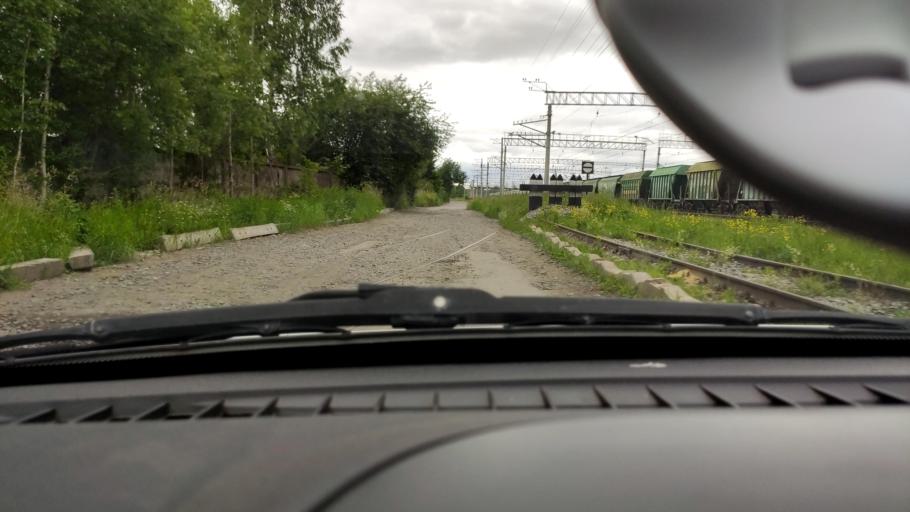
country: RU
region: Perm
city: Ferma
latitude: 57.8910
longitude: 56.2990
